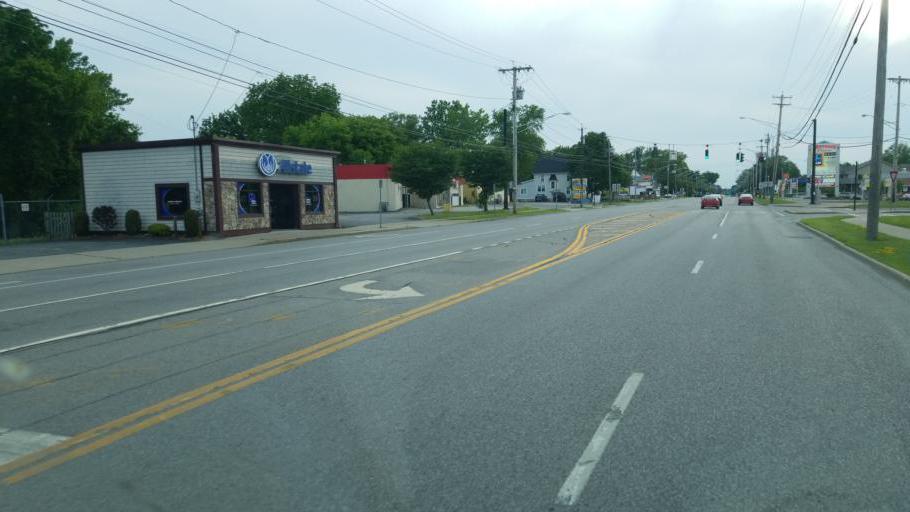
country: US
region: New York
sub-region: Genesee County
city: Batavia
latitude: 42.9949
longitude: -78.1632
